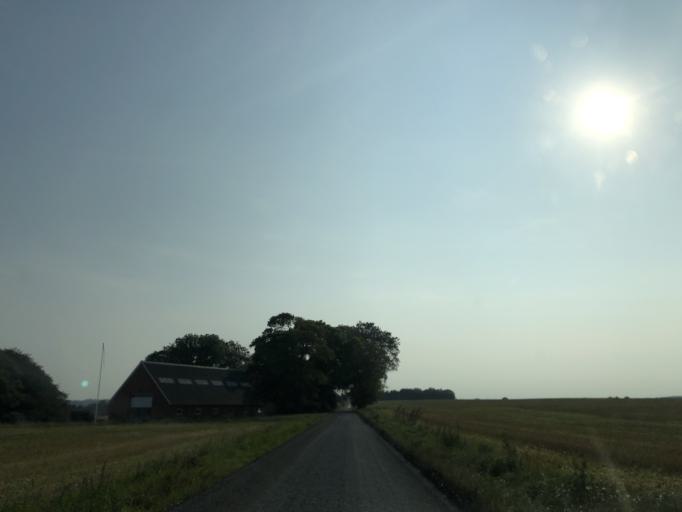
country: DK
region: Central Jutland
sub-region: Favrskov Kommune
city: Hammel
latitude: 56.2401
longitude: 9.7607
